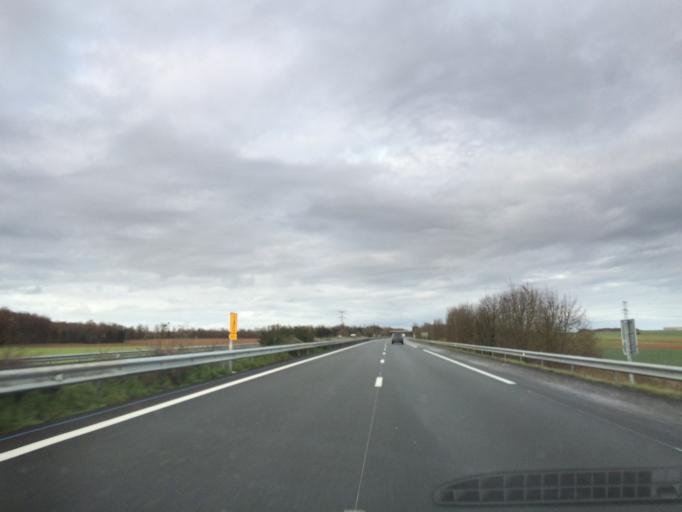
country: FR
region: Poitou-Charentes
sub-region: Departement des Deux-Sevres
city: Beauvoir-sur-Niort
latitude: 46.1626
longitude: -0.5139
